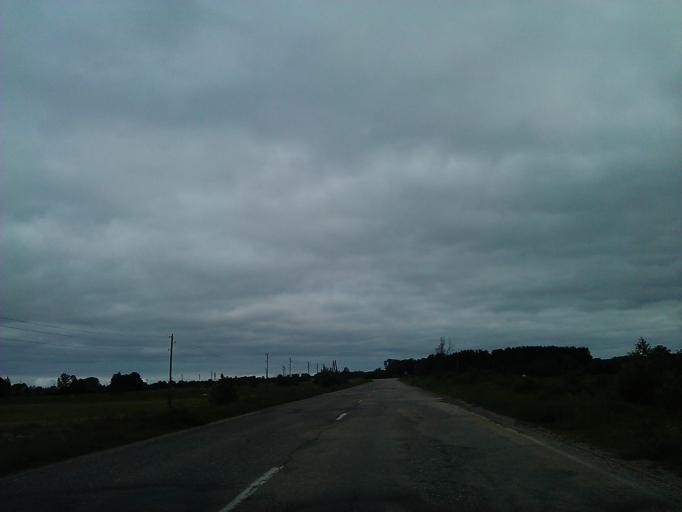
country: LV
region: Adazi
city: Adazi
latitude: 57.1101
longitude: 24.3079
